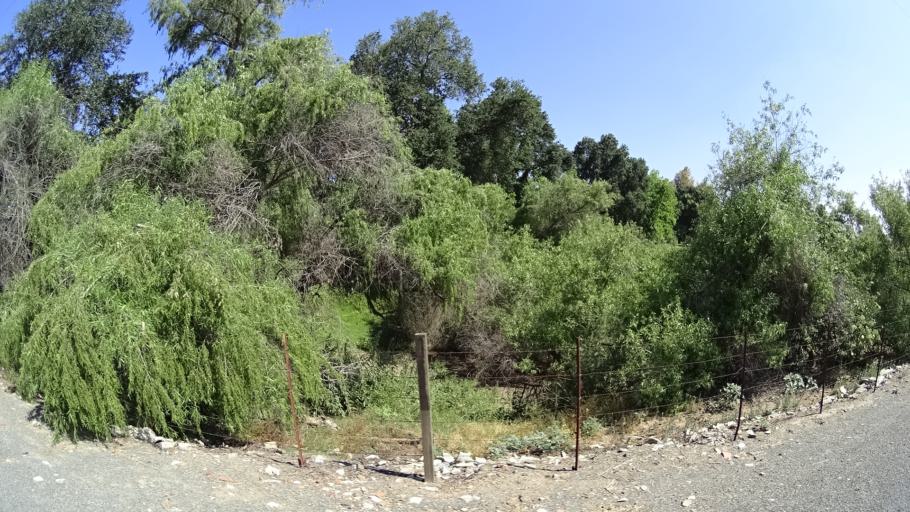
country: US
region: California
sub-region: Fresno County
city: Kingsburg
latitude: 36.4524
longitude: -119.5760
